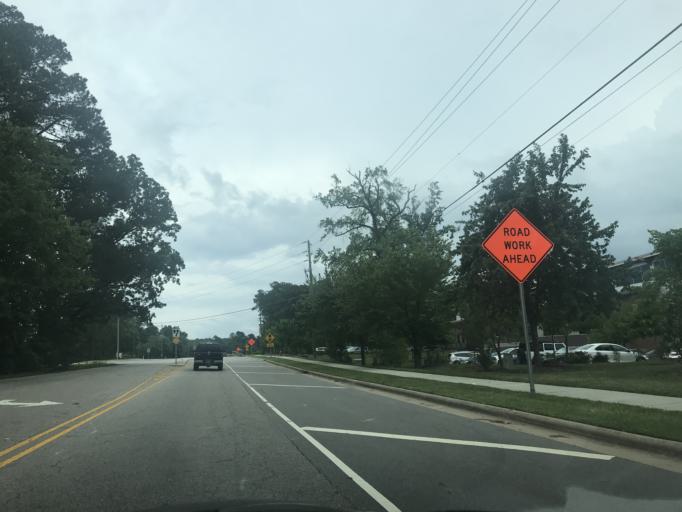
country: US
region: North Carolina
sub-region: Wake County
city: Green Level
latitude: 35.8242
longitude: -78.8784
